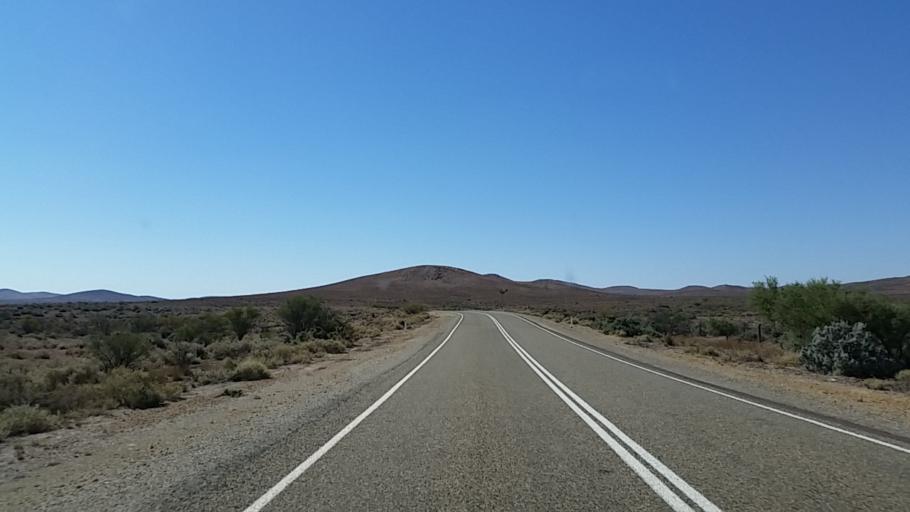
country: AU
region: South Australia
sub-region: Flinders Ranges
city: Quorn
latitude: -32.2518
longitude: 138.5131
